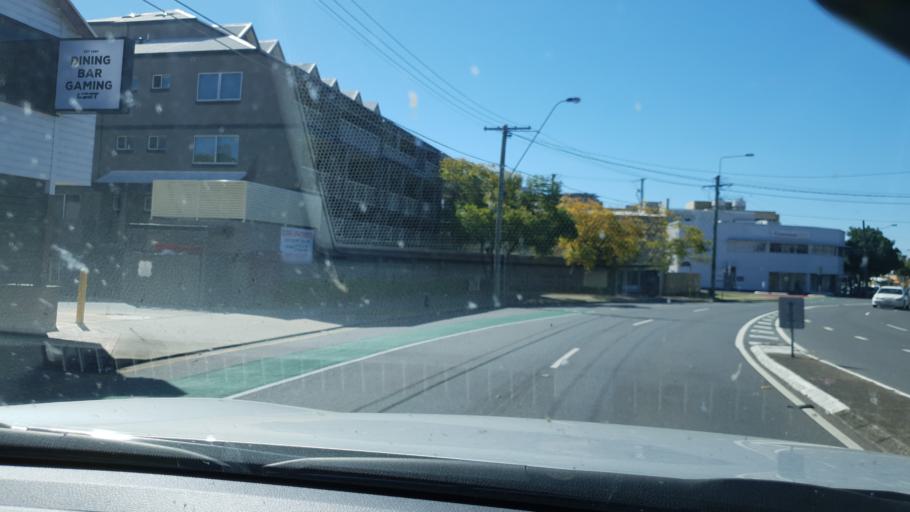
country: AU
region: Queensland
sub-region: Brisbane
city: Woolloongabba
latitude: -27.4898
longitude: 153.0273
